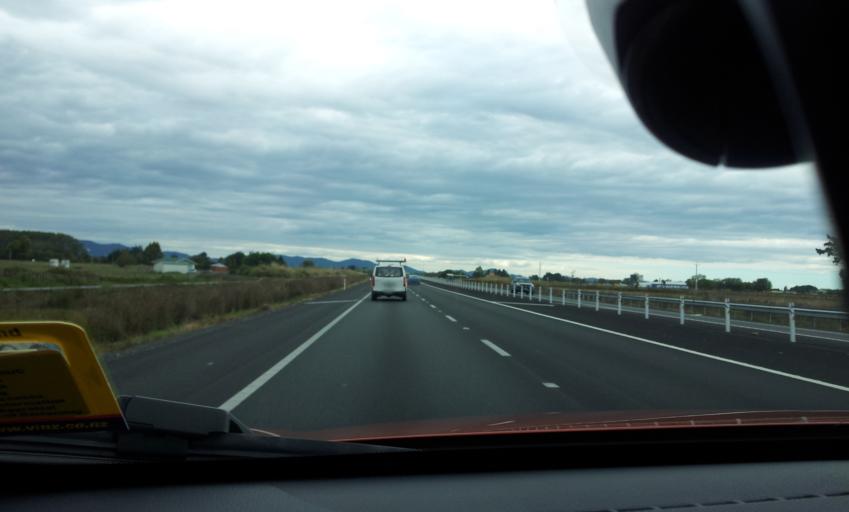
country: NZ
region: Waikato
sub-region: Hamilton City
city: Hamilton
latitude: -37.7452
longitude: 175.2145
